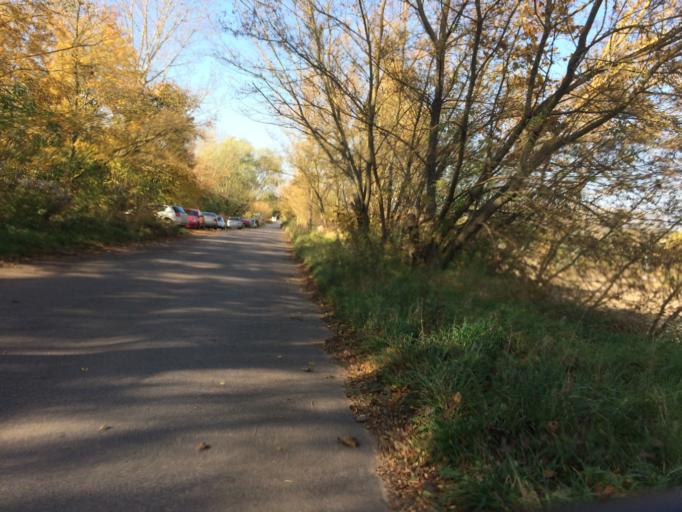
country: DE
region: Berlin
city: Blankenfelde
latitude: 52.6381
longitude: 13.4152
